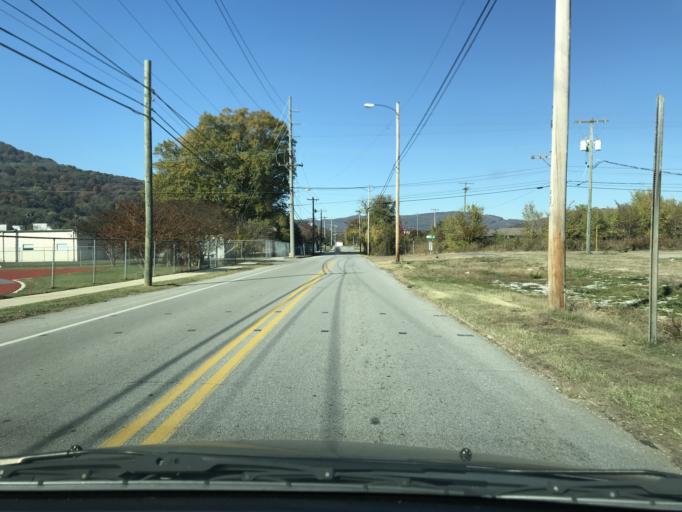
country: US
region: Tennessee
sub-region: Hamilton County
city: Chattanooga
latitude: 35.0167
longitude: -85.3195
